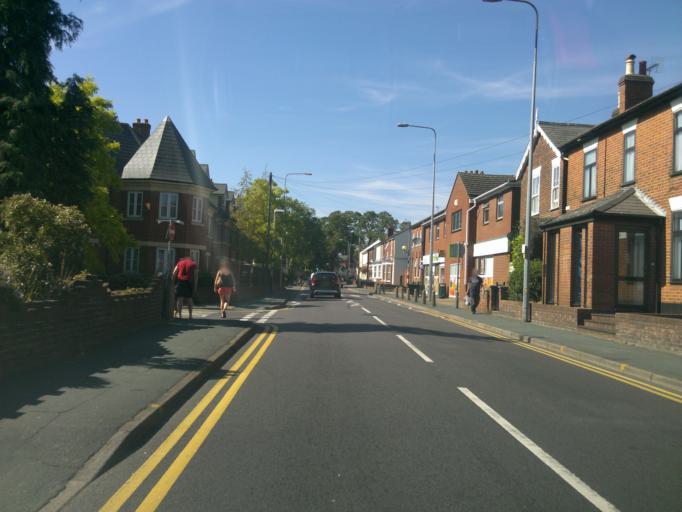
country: GB
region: England
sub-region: Essex
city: Colchester
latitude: 51.8792
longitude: 0.9059
